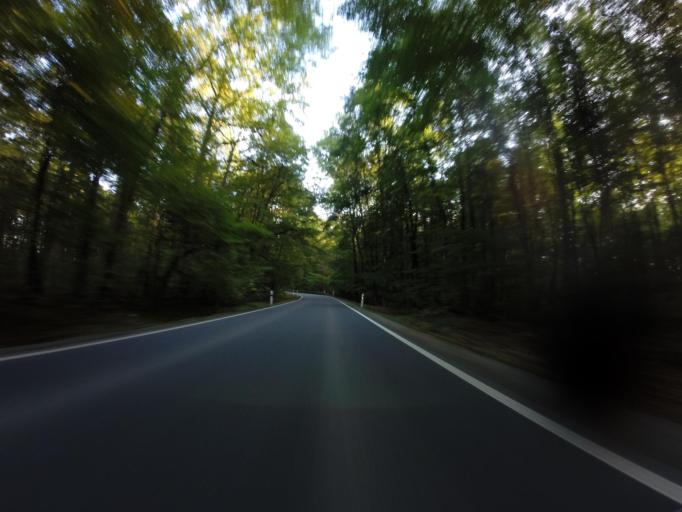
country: DE
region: Thuringia
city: Lehesten
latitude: 50.9613
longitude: 11.5423
